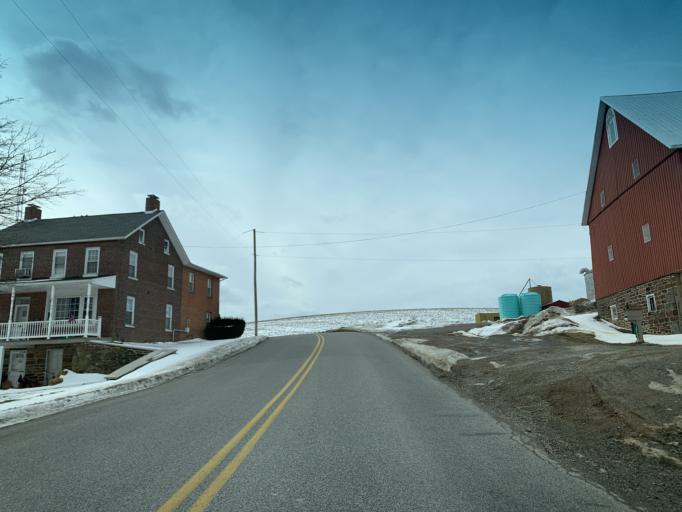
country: US
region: Pennsylvania
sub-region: York County
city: Shrewsbury
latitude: 39.7793
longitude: -76.6456
